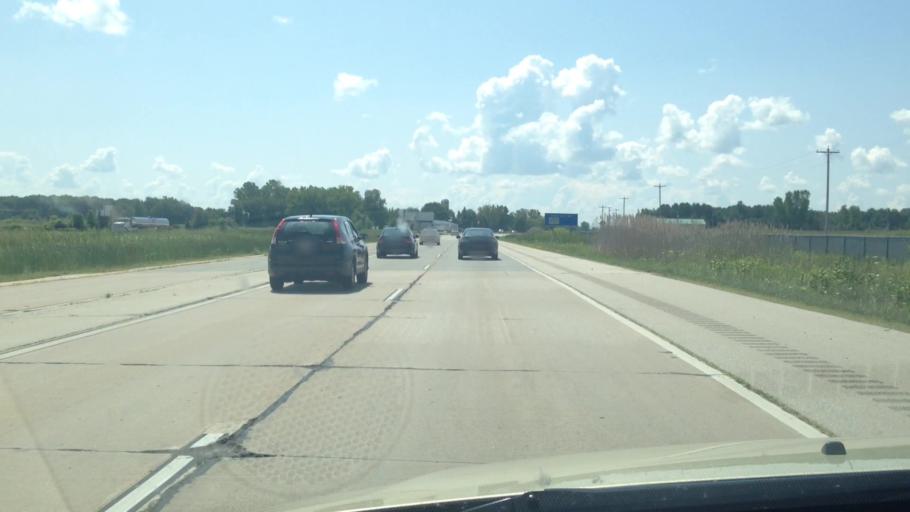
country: US
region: Wisconsin
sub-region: Brown County
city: Suamico
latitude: 44.7396
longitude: -88.0519
